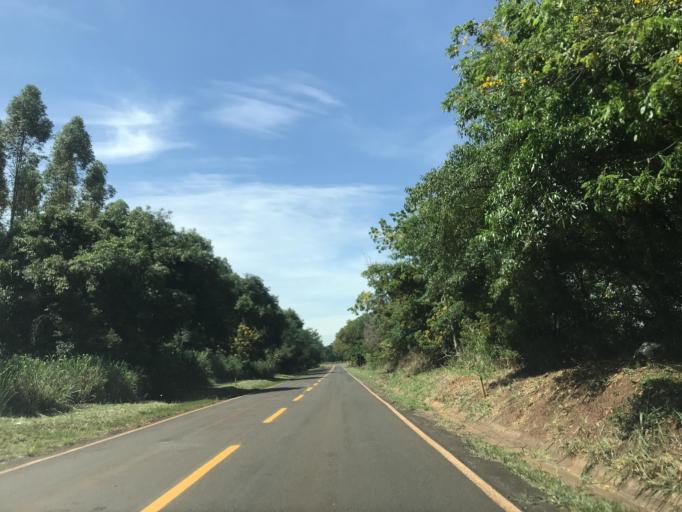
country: BR
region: Parana
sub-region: Terra Rica
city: Terra Rica
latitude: -22.7902
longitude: -52.6545
